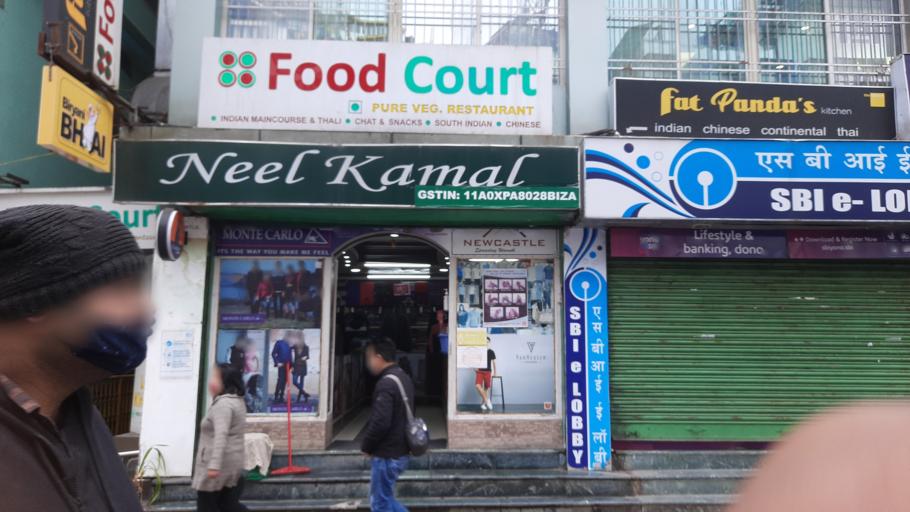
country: IN
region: Sikkim
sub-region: East District
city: Gangtok
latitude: 27.3285
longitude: 88.6124
